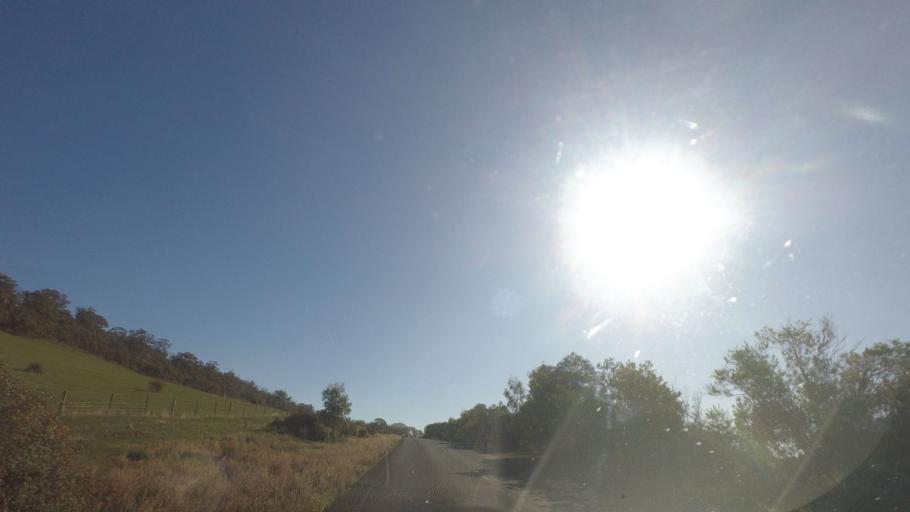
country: AU
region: Victoria
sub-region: Mount Alexander
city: Castlemaine
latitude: -37.0382
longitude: 144.2783
